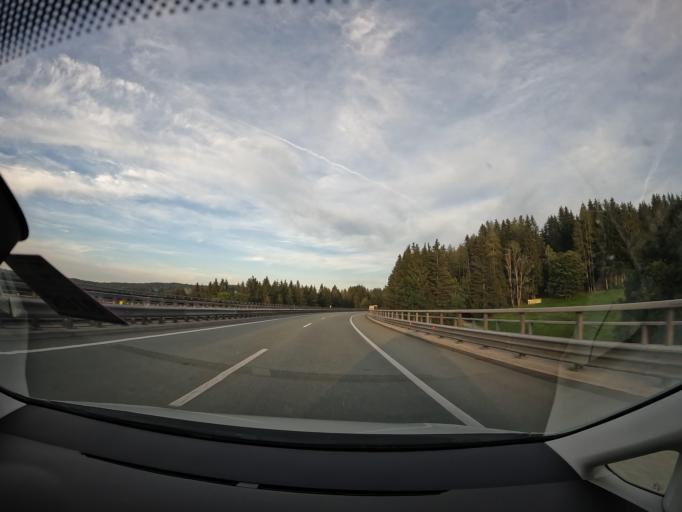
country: AT
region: Styria
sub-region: Politischer Bezirk Voitsberg
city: Modriach
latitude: 46.9553
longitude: 15.0231
